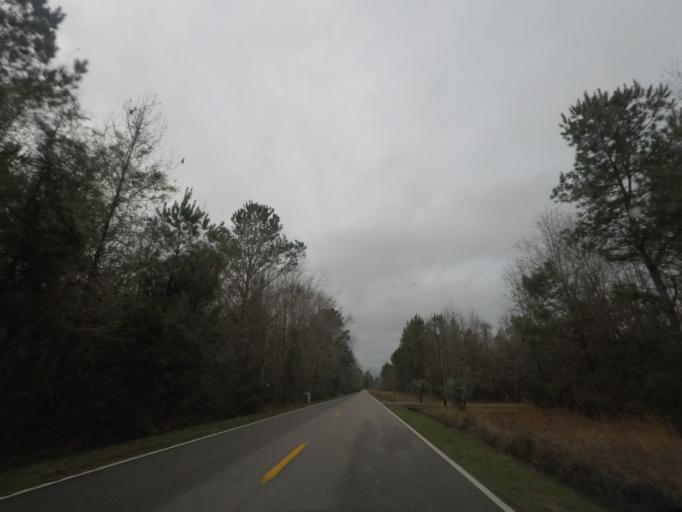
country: US
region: South Carolina
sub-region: Colleton County
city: Walterboro
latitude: 32.8855
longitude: -80.5071
